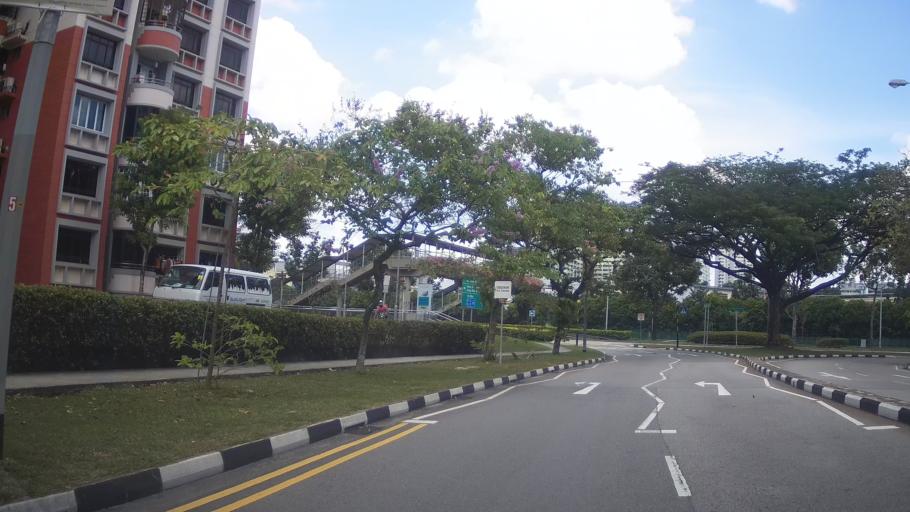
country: MY
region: Johor
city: Johor Bahru
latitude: 1.3417
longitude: 103.7080
